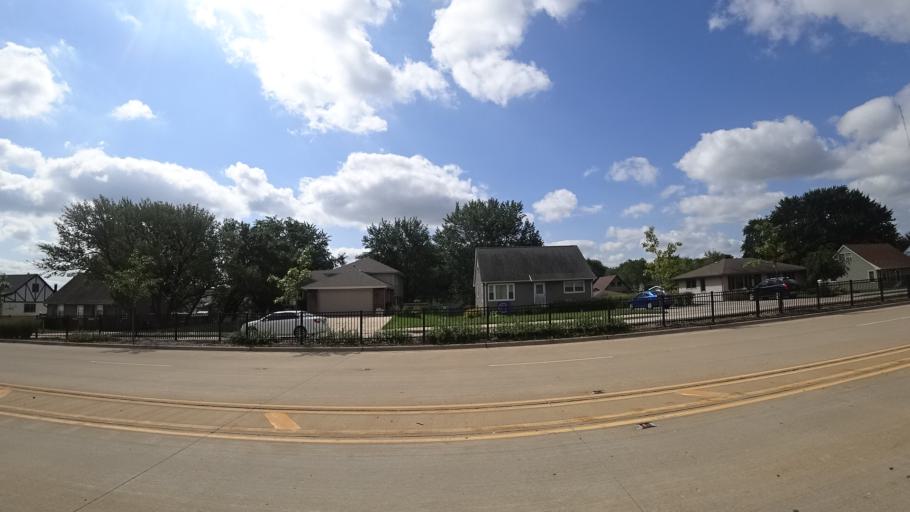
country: US
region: Illinois
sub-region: Cook County
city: Orland Hills
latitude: 41.5579
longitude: -87.8426
